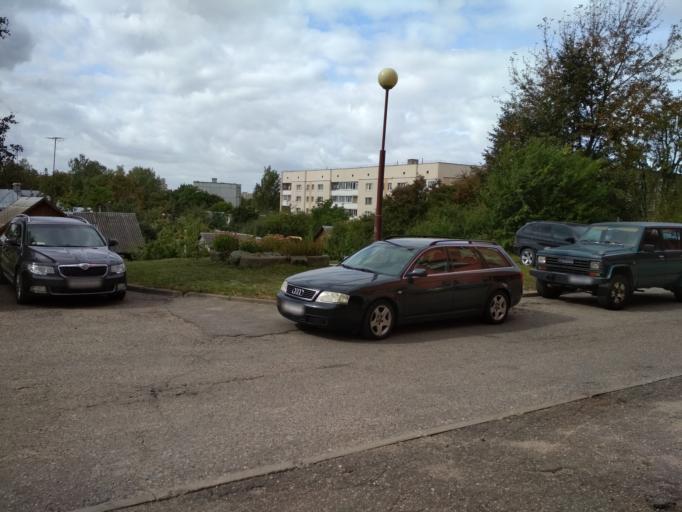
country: BY
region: Grodnenskaya
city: Hrodna
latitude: 53.6958
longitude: 23.8204
